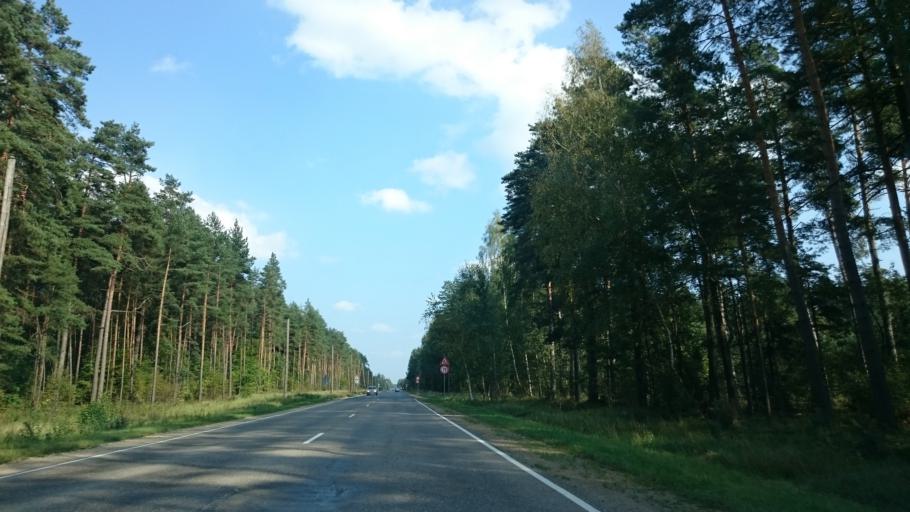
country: LV
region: Stopini
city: Ulbroka
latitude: 56.9454
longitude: 24.3045
